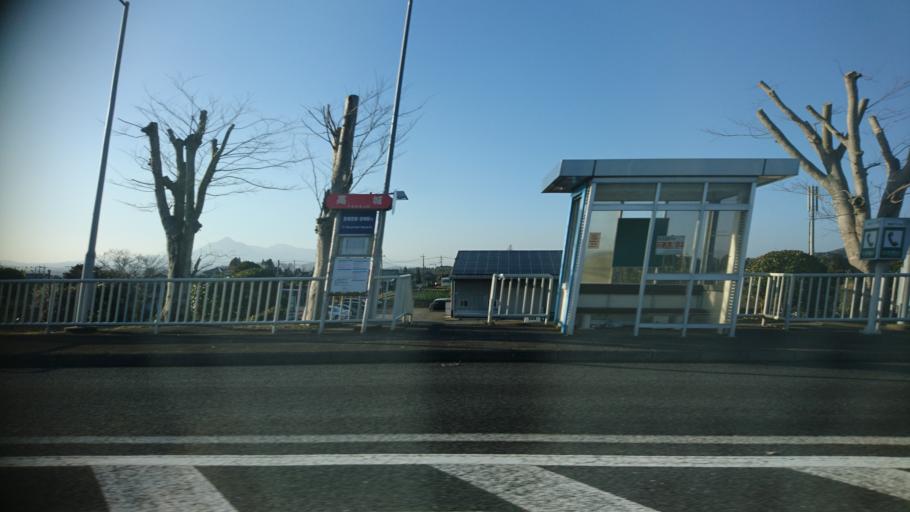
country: JP
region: Miyazaki
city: Miyakonojo
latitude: 31.7889
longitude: 131.1514
